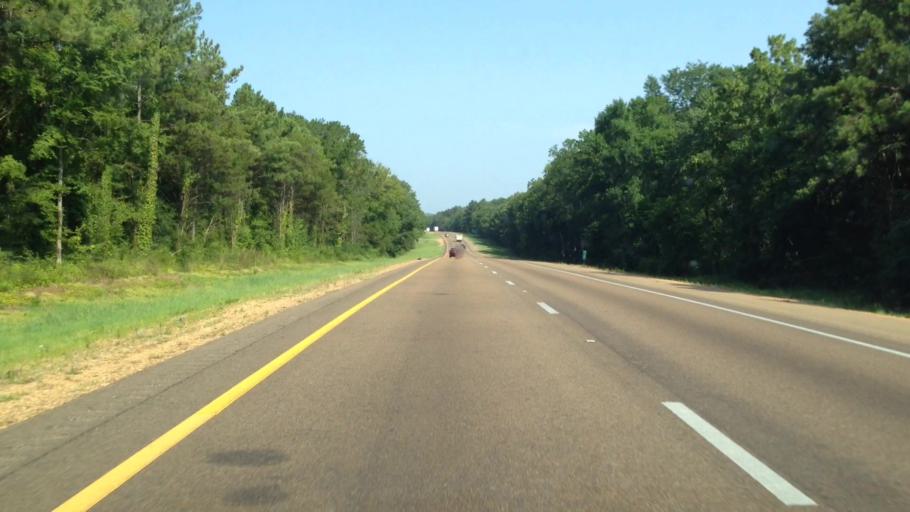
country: US
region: Mississippi
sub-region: Hinds County
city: Clinton
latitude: 32.3092
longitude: -90.2943
